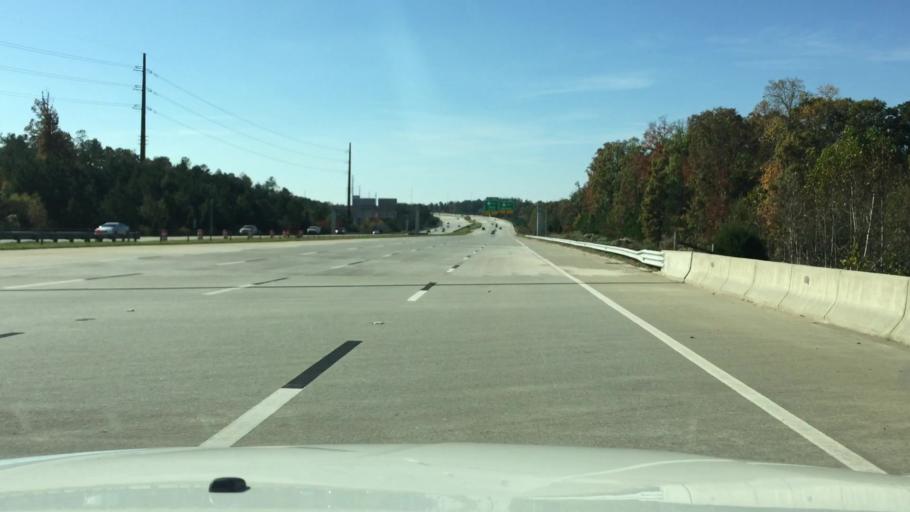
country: US
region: North Carolina
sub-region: Wake County
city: Morrisville
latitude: 35.8470
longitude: -78.8708
